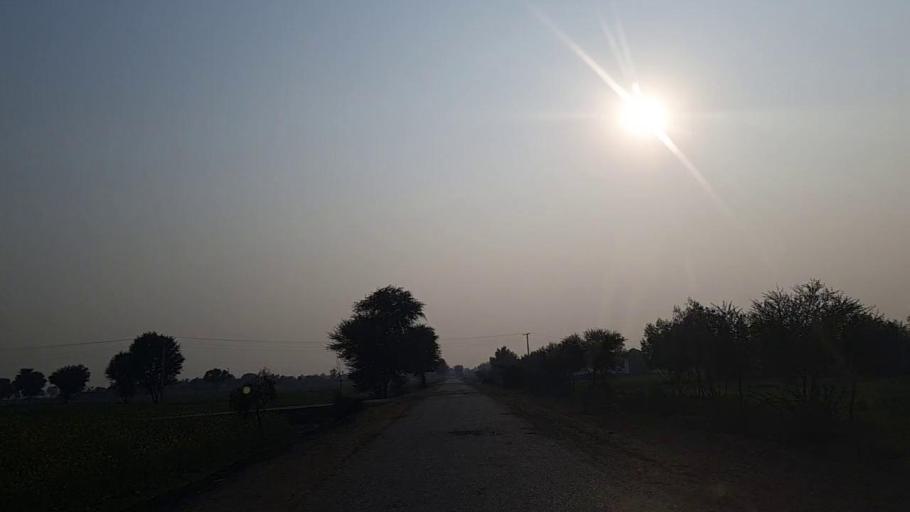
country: PK
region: Sindh
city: Nawabshah
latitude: 26.2219
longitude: 68.4768
